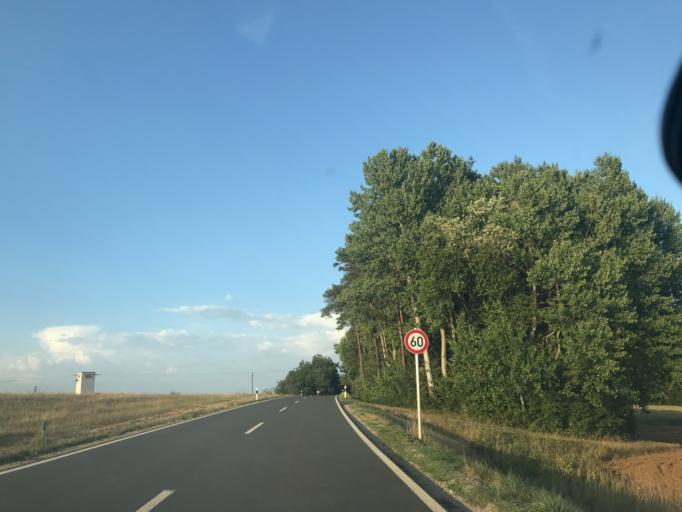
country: DE
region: Bavaria
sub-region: Upper Franconia
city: Obertrubach
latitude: 49.7015
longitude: 11.3996
